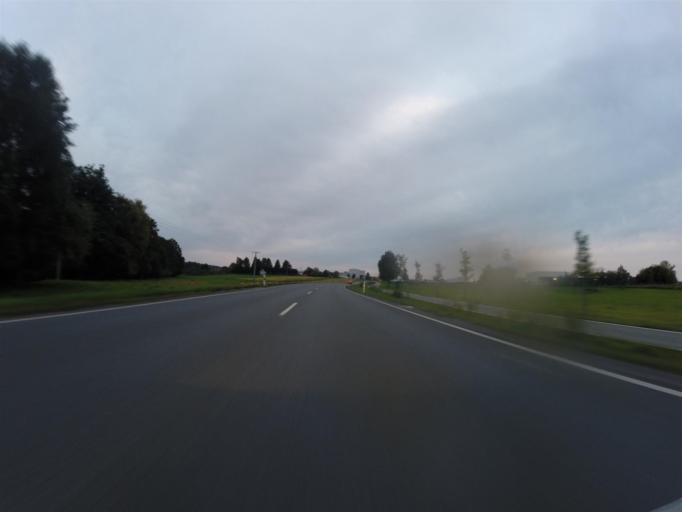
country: DE
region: Thuringia
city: Petersberg
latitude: 50.9673
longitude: 11.8450
